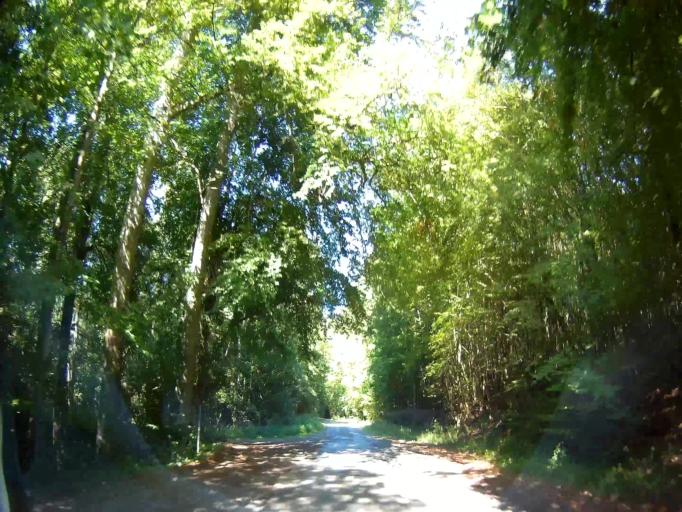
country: BE
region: Wallonia
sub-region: Province de Namur
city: Houyet
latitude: 50.2246
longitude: 4.9800
